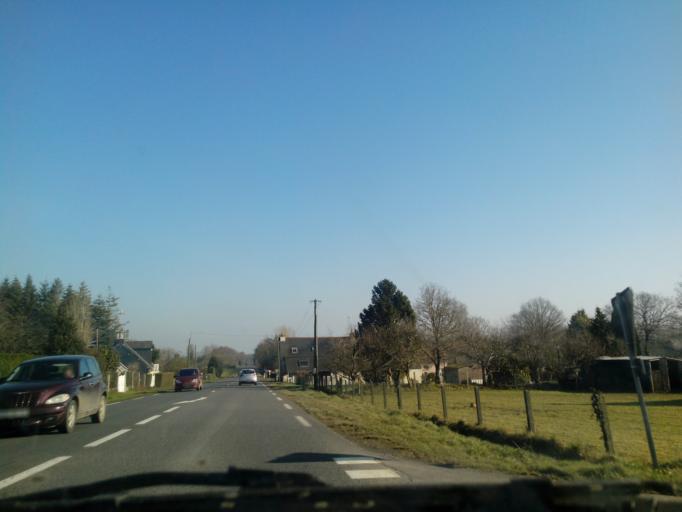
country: FR
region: Brittany
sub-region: Departement des Cotes-d'Armor
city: Merdrignac
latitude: 48.1950
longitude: -2.4560
